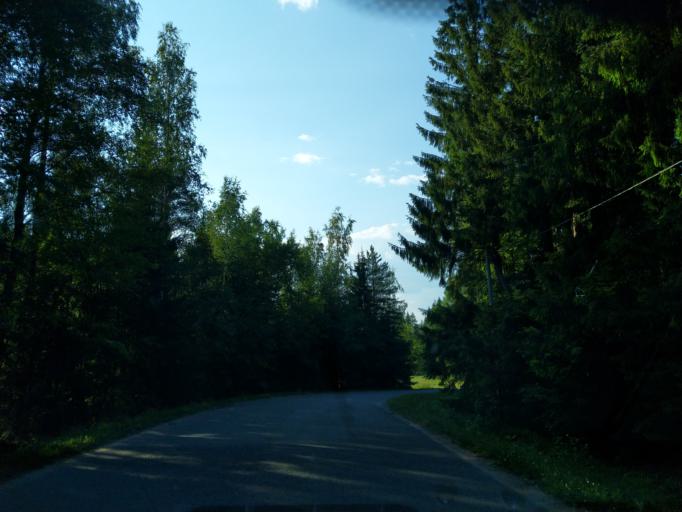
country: FI
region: Satakunta
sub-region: Pori
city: Laengelmaeki
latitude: 61.8082
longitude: 22.1898
